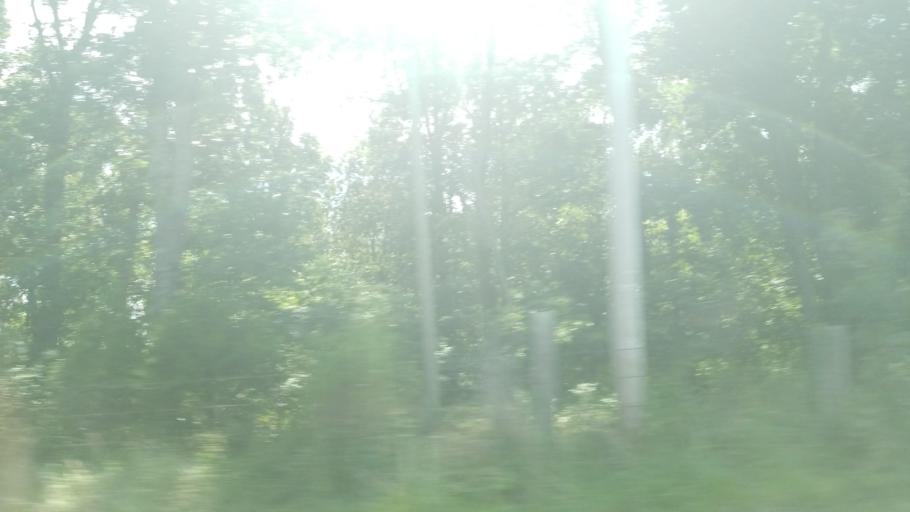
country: US
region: Illinois
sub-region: Williamson County
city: Johnston City
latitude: 37.7869
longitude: -88.7879
